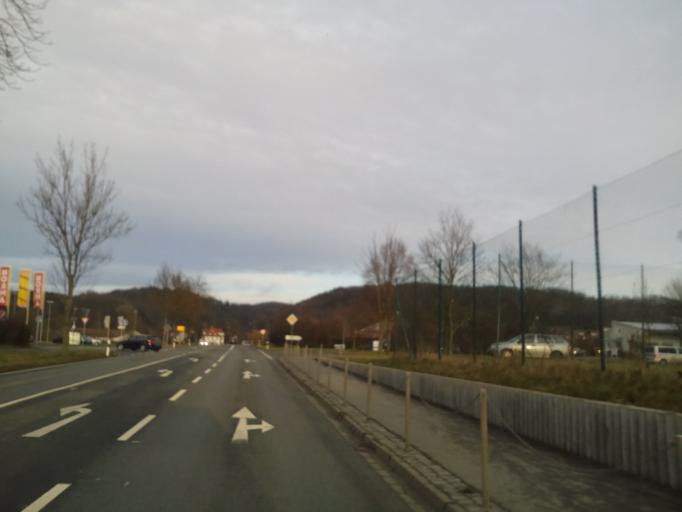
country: DE
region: Bavaria
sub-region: Upper Franconia
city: Neuenmarkt
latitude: 50.0979
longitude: 11.5903
